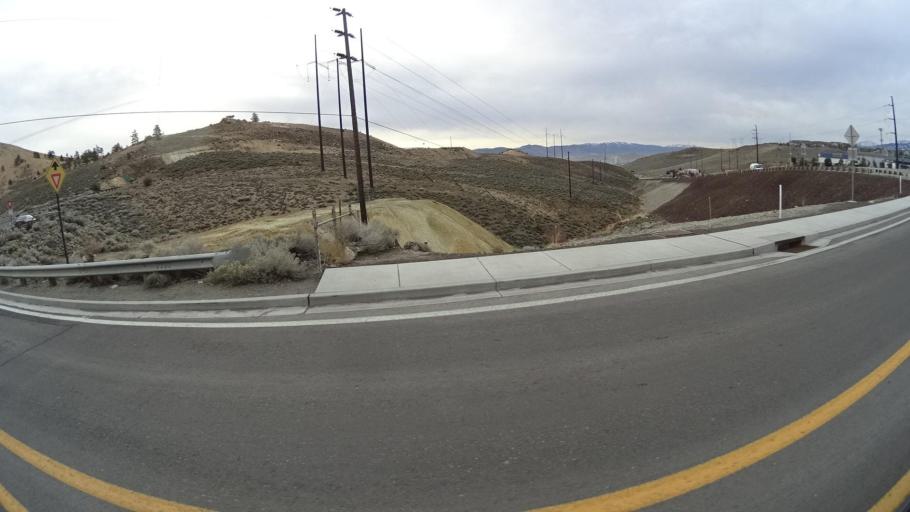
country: US
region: Nevada
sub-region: Washoe County
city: Sun Valley
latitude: 39.5749
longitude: -119.8077
